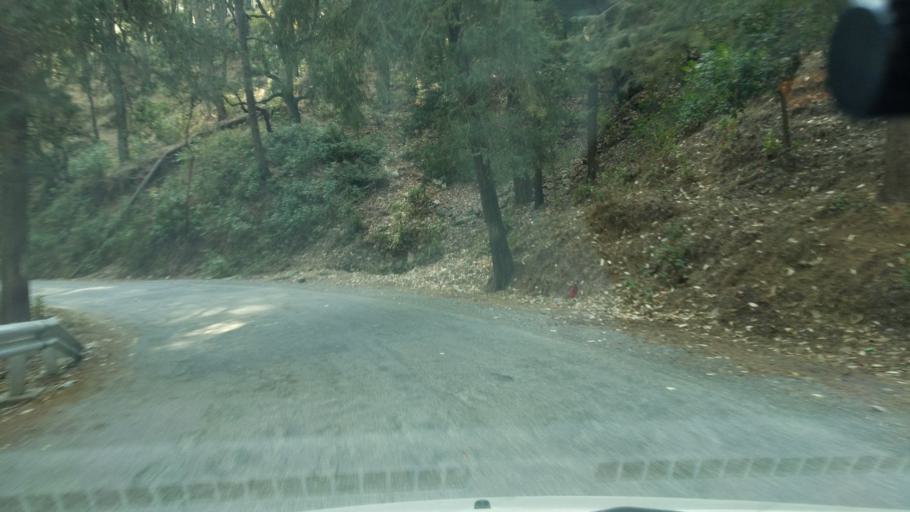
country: IN
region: Uttarakhand
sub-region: Naini Tal
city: Bhowali
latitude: 29.3979
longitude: 79.5380
